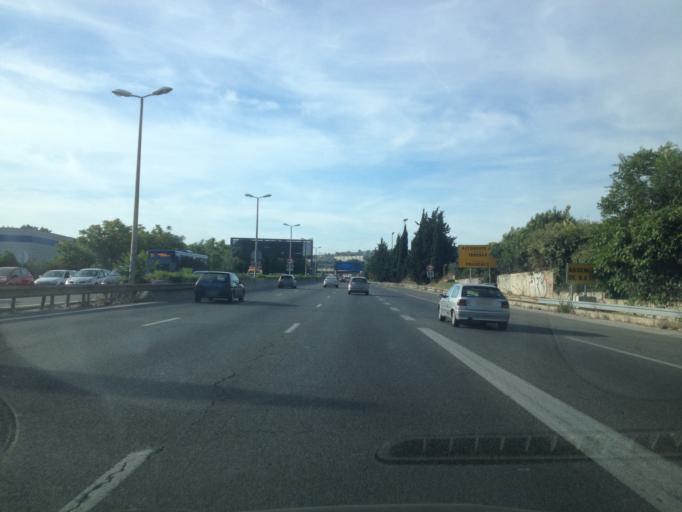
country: FR
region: Provence-Alpes-Cote d'Azur
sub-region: Departement des Bouches-du-Rhone
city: Marseille 14
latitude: 43.3345
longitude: 5.3774
